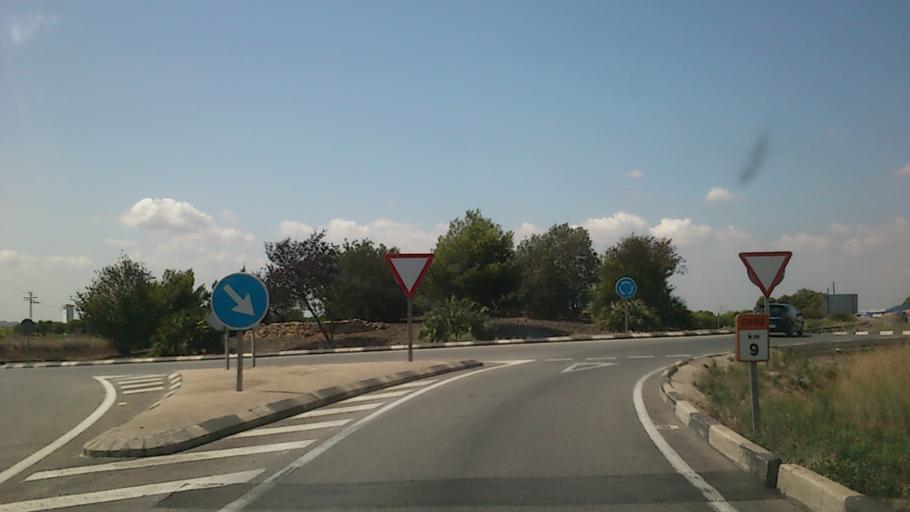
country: ES
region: Valencia
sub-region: Provincia de Valencia
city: Museros
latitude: 39.5949
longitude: -0.3696
